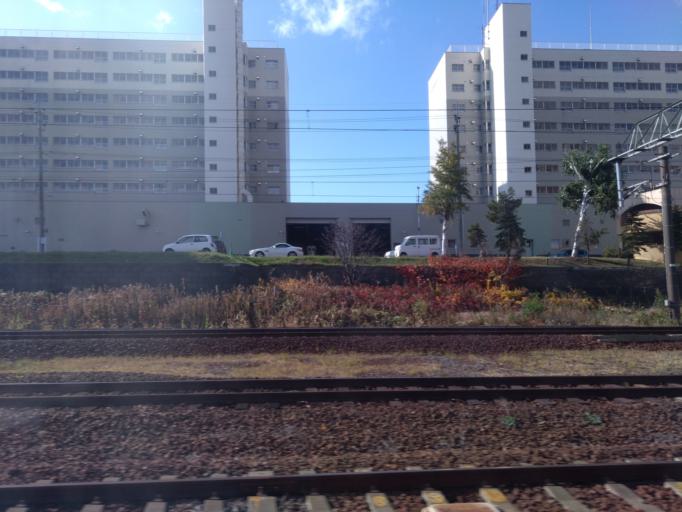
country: JP
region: Hokkaido
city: Kitahiroshima
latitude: 42.9775
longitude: 141.5635
